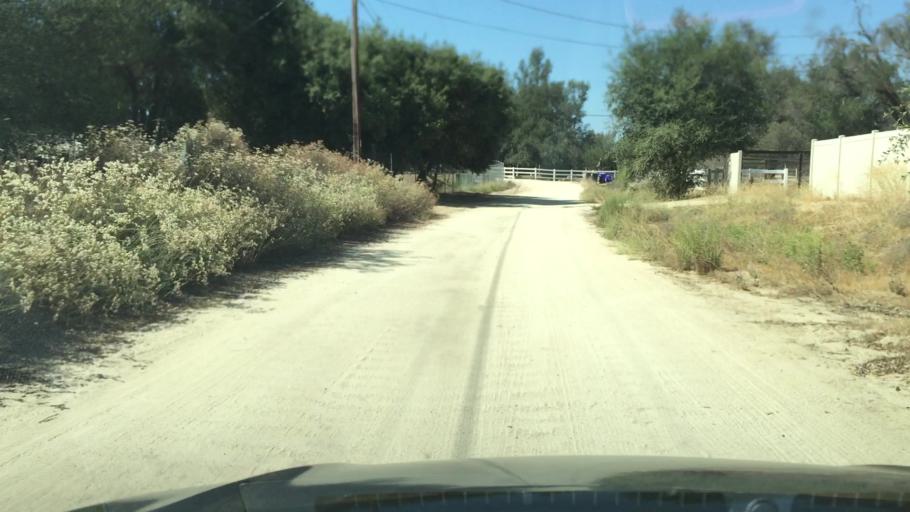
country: US
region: California
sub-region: San Diego County
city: Alpine
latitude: 32.7547
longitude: -116.7551
